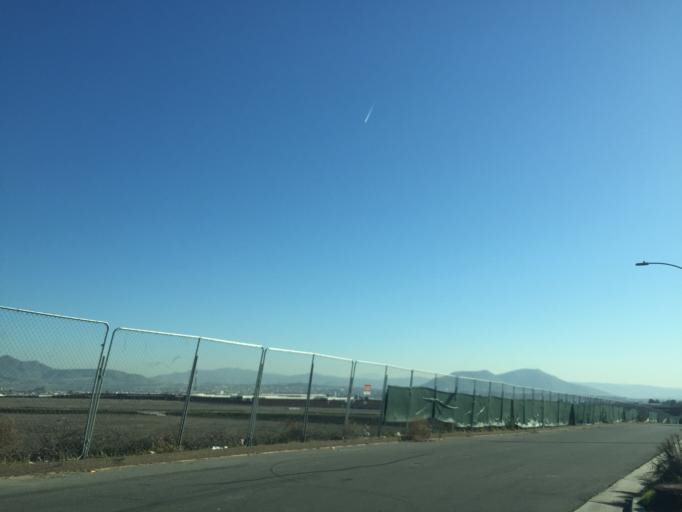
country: MX
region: Baja California
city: Tijuana
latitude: 32.5584
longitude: -116.9235
